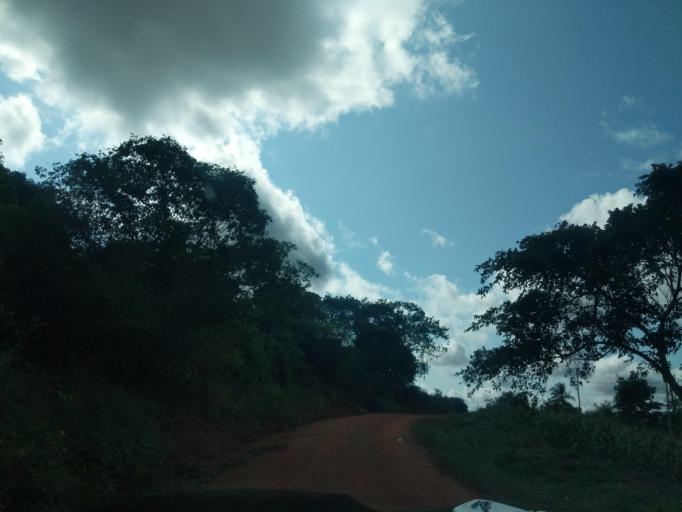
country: TZ
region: Tanga
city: Muheza
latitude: -5.4190
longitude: 38.6245
